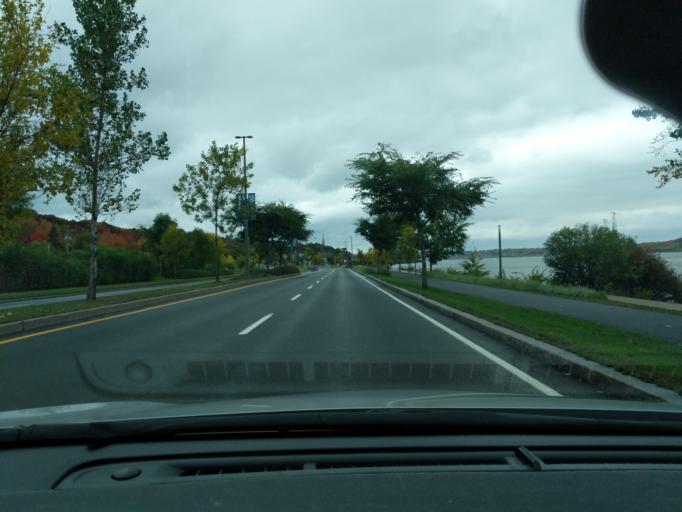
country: CA
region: Quebec
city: Quebec
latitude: 46.7655
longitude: -71.2601
